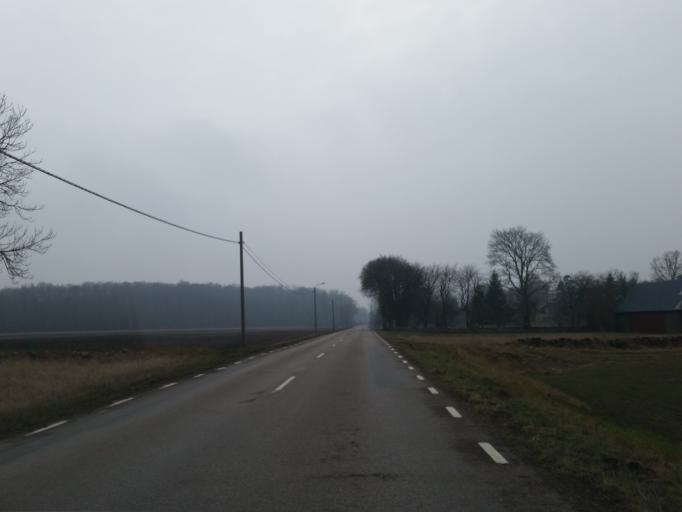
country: SE
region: Kalmar
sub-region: Morbylanga Kommun
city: Moerbylanga
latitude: 56.4333
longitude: 16.4192
